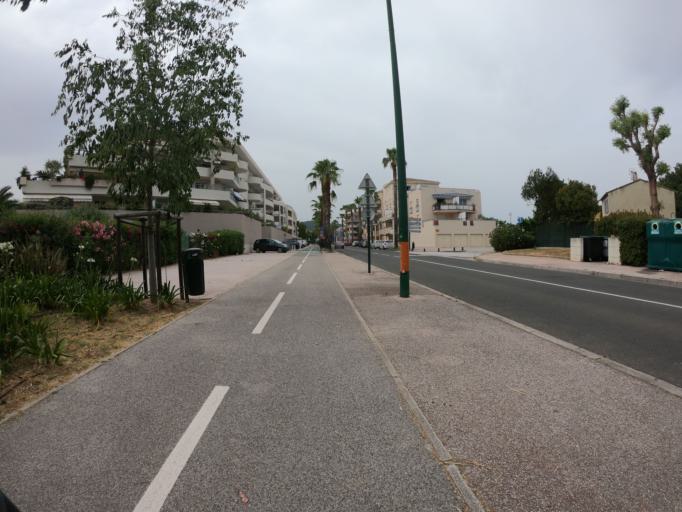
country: FR
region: Provence-Alpes-Cote d'Azur
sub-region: Departement du Var
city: La Garde
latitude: 43.1299
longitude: 6.0195
